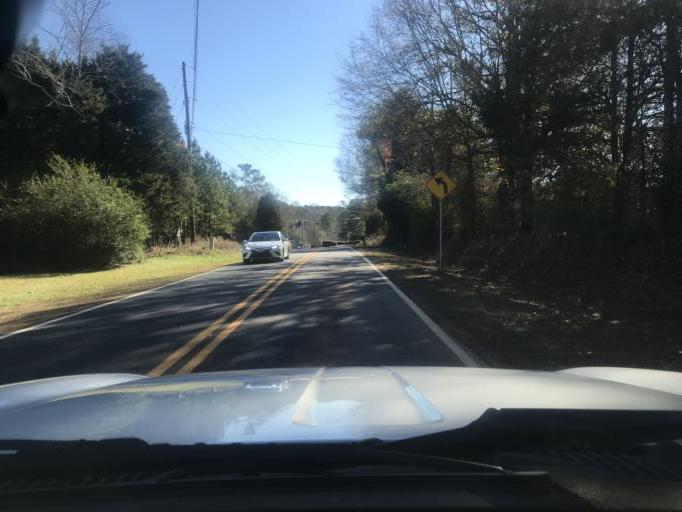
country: US
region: Georgia
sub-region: Barrow County
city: Winder
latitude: 33.9143
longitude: -83.7604
